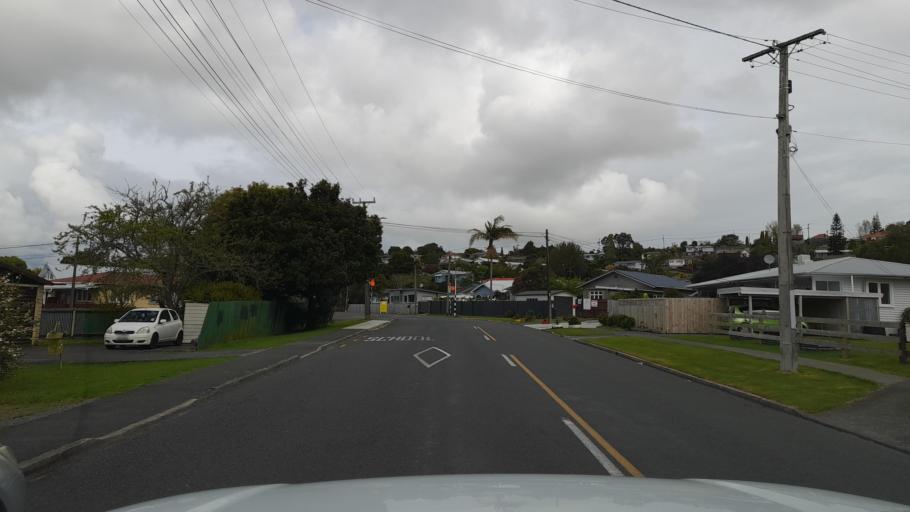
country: NZ
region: Northland
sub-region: Whangarei
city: Whangarei
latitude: -35.7351
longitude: 174.3214
